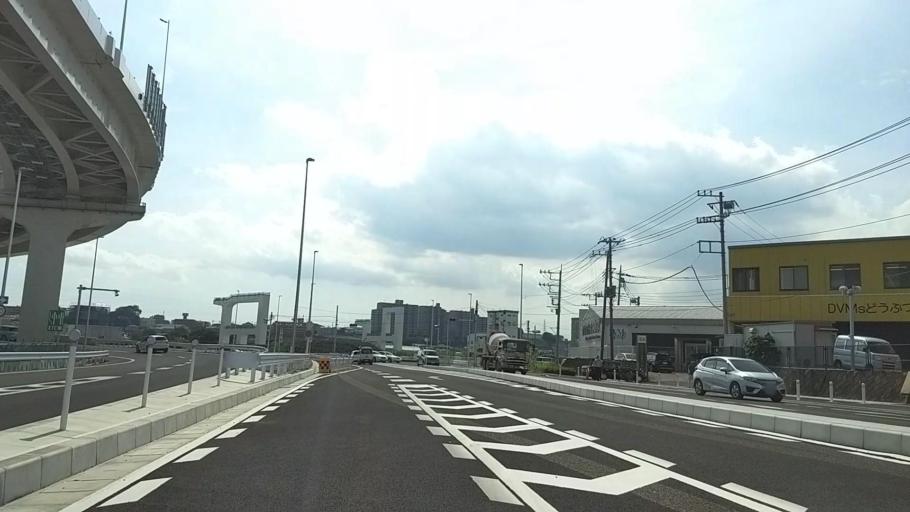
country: JP
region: Kanagawa
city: Yokohama
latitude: 35.5173
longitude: 139.5906
